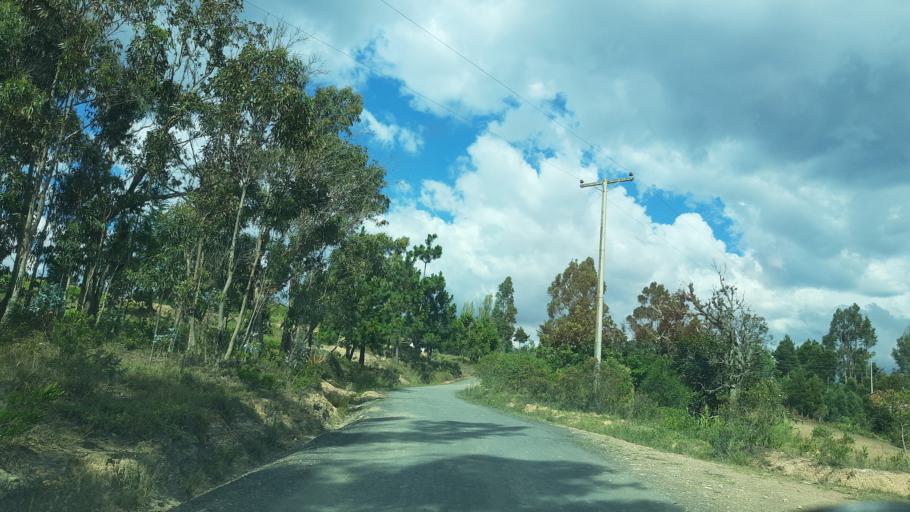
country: CO
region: Boyaca
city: La Capilla
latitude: 5.7094
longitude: -73.5382
